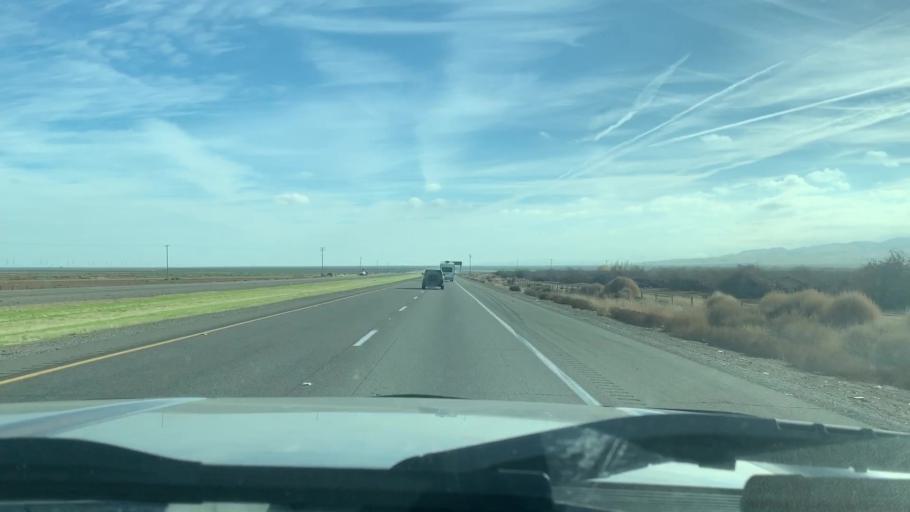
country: US
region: California
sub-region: Merced County
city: South Dos Palos
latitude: 36.8138
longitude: -120.7491
